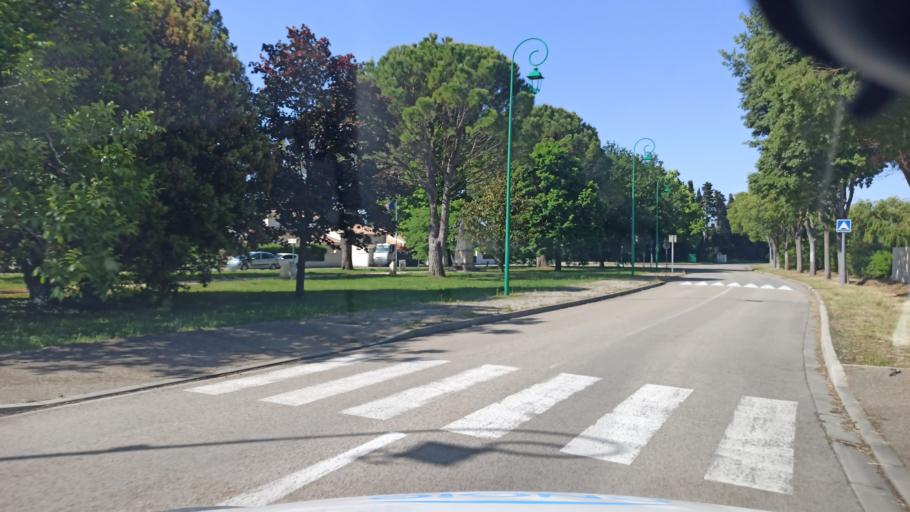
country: FR
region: Provence-Alpes-Cote d'Azur
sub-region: Departement des Bouches-du-Rhone
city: Saint-Andiol
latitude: 43.8401
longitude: 4.9176
